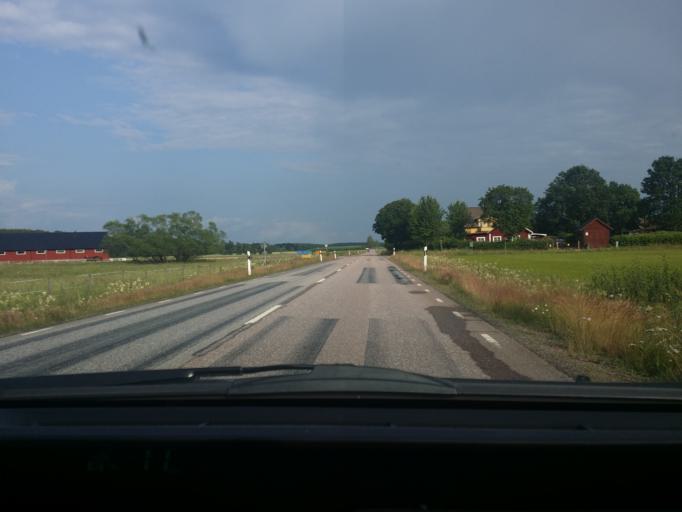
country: SE
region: Vaestmanland
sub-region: Hallstahammars Kommun
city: Kolback
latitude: 59.5624
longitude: 16.3121
